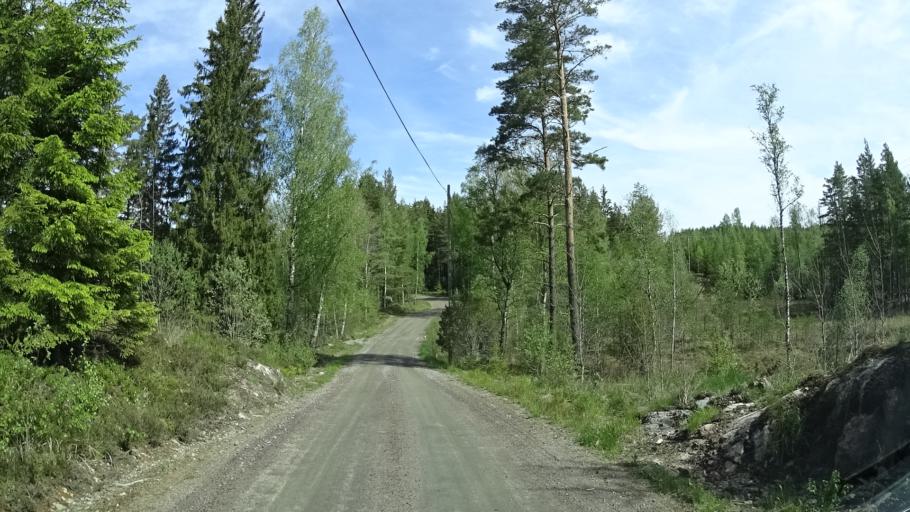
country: SE
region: OEstergoetland
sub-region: Finspangs Kommun
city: Finspang
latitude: 58.7557
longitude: 15.8355
